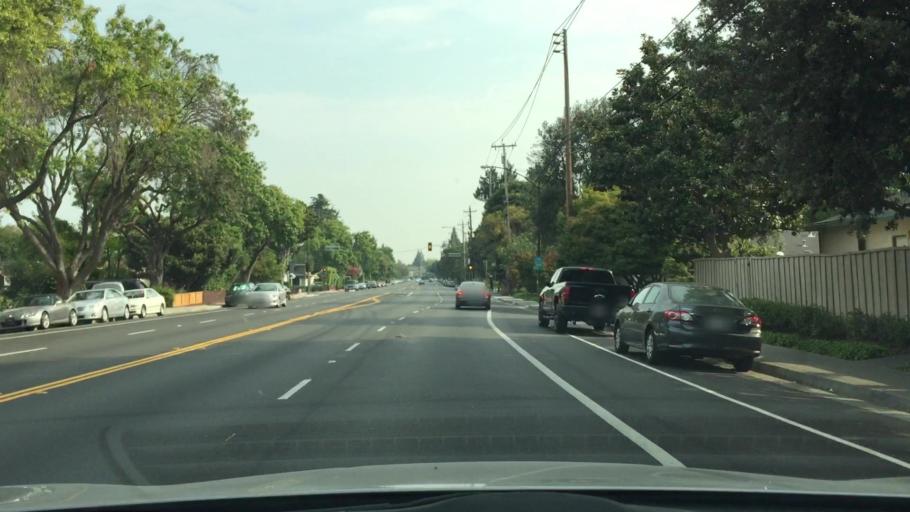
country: US
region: California
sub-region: Santa Clara County
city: Mountain View
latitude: 37.4059
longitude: -122.0957
